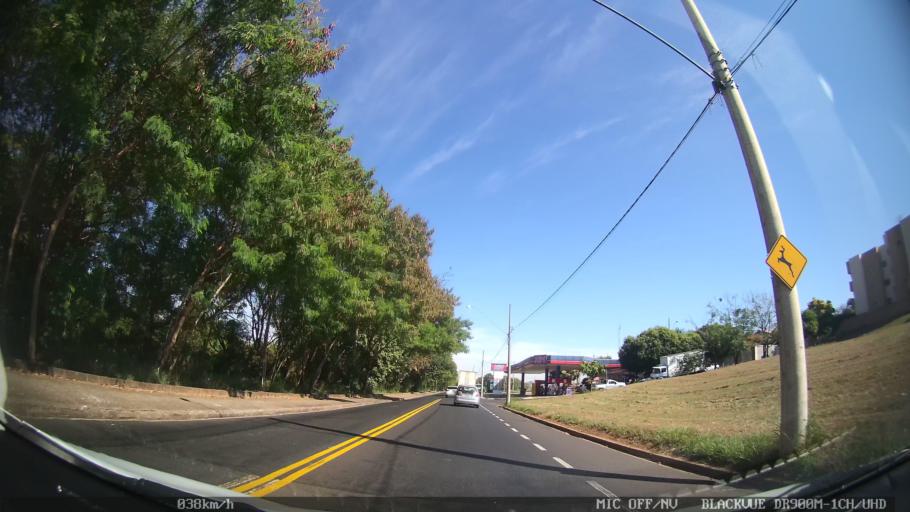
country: BR
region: Sao Paulo
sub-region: Sao Jose Do Rio Preto
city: Sao Jose do Rio Preto
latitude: -20.8030
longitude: -49.4106
